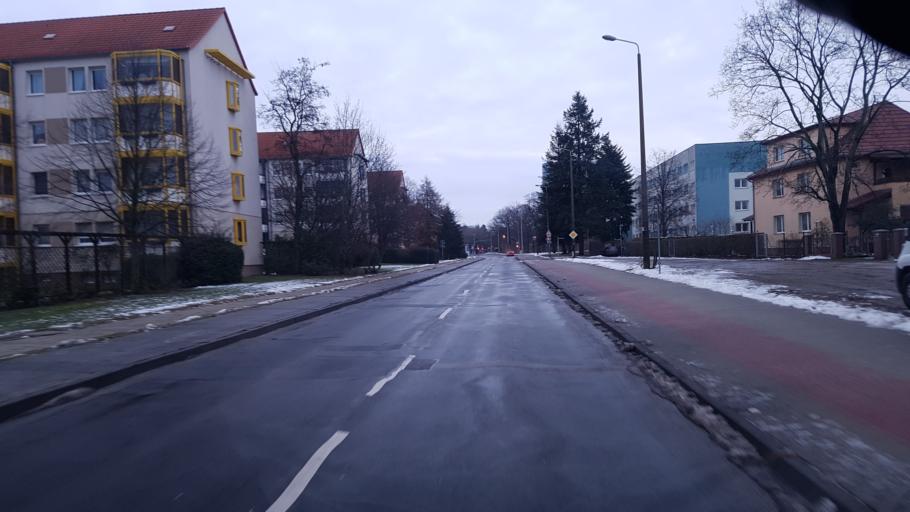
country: DE
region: Brandenburg
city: Cottbus
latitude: 51.7380
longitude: 14.3289
